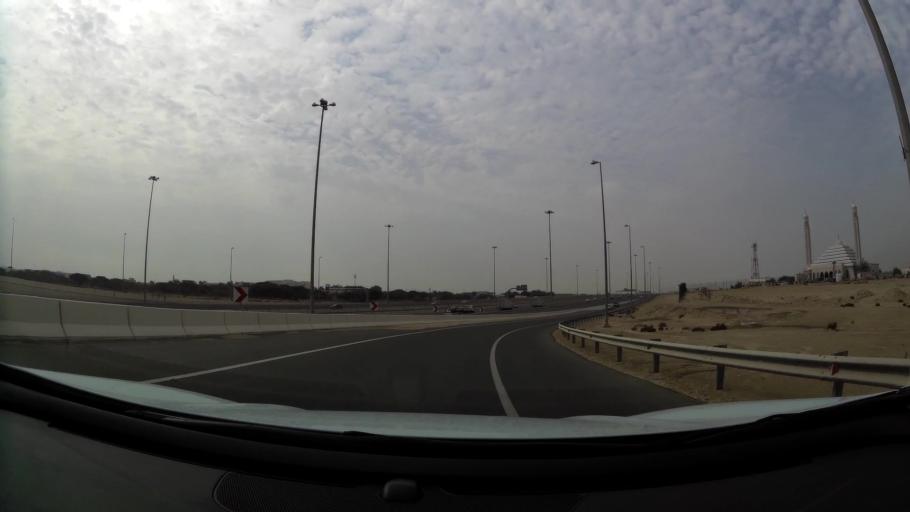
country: AE
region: Abu Dhabi
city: Abu Dhabi
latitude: 24.6857
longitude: 54.7718
